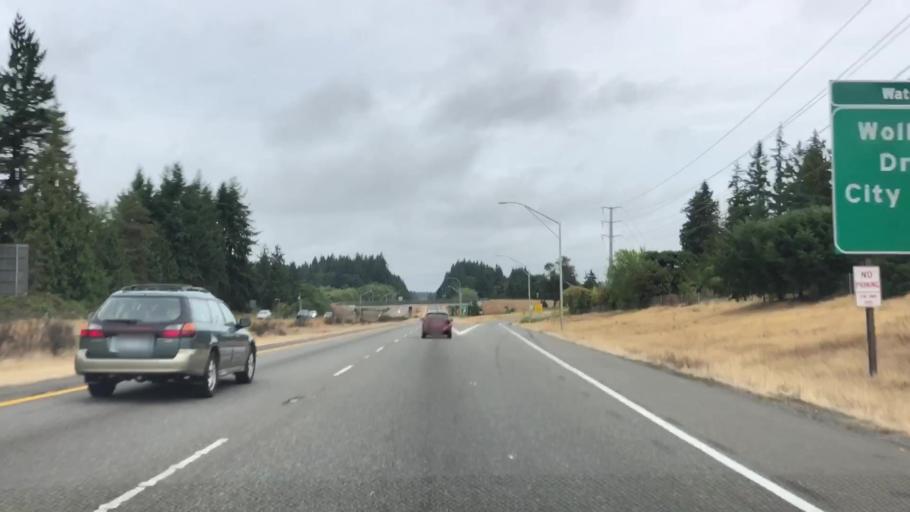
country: US
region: Washington
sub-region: Pierce County
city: Gig Harbor
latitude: 47.3175
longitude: -122.5871
